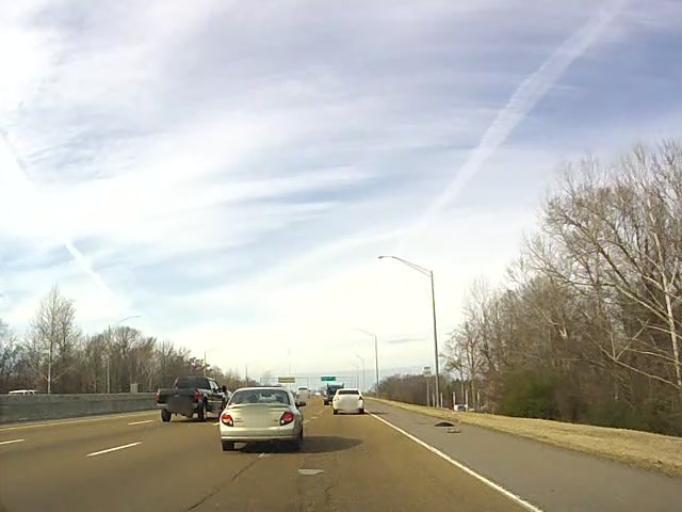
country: US
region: Tennessee
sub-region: Shelby County
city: Germantown
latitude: 35.0698
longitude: -89.8513
